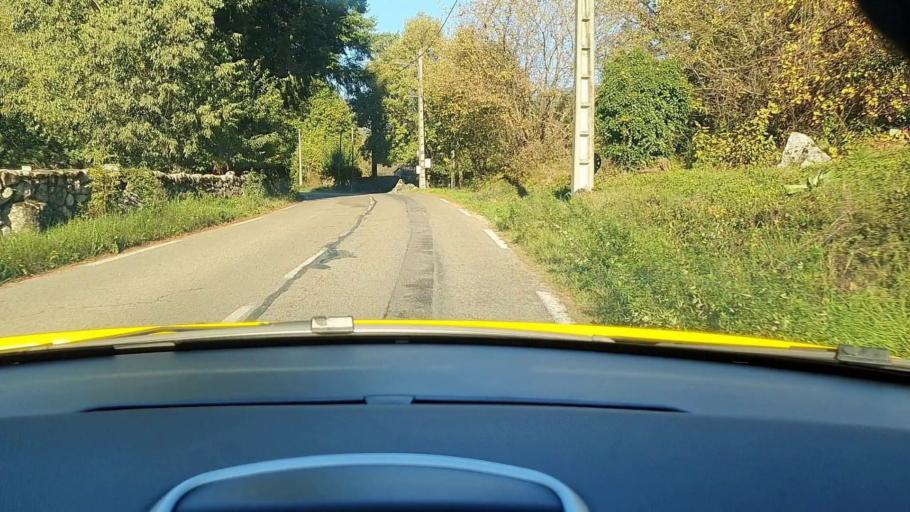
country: FR
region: Languedoc-Roussillon
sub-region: Departement du Gard
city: Le Vigan
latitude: 43.9852
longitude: 3.5832
